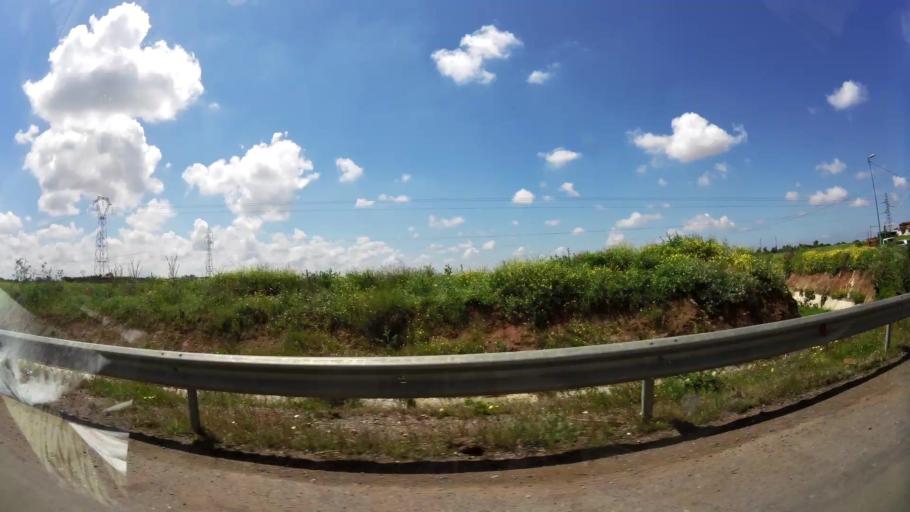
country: MA
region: Grand Casablanca
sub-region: Casablanca
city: Casablanca
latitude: 33.5165
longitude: -7.6146
